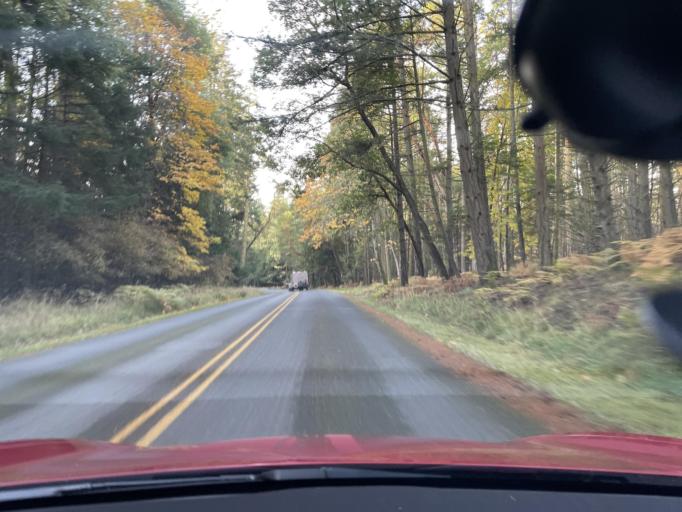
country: US
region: Washington
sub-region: San Juan County
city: Friday Harbor
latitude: 48.5359
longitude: -123.1587
